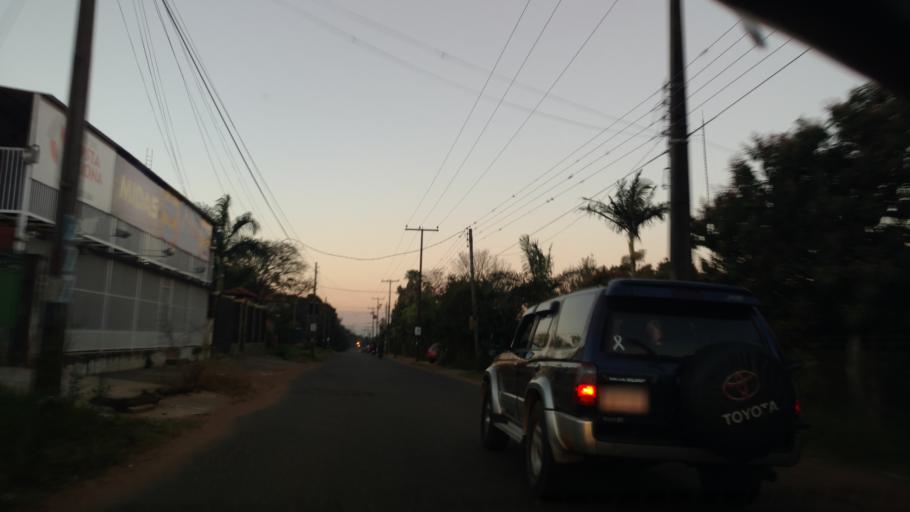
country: PY
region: Central
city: Guarambare
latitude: -25.4745
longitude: -57.4124
